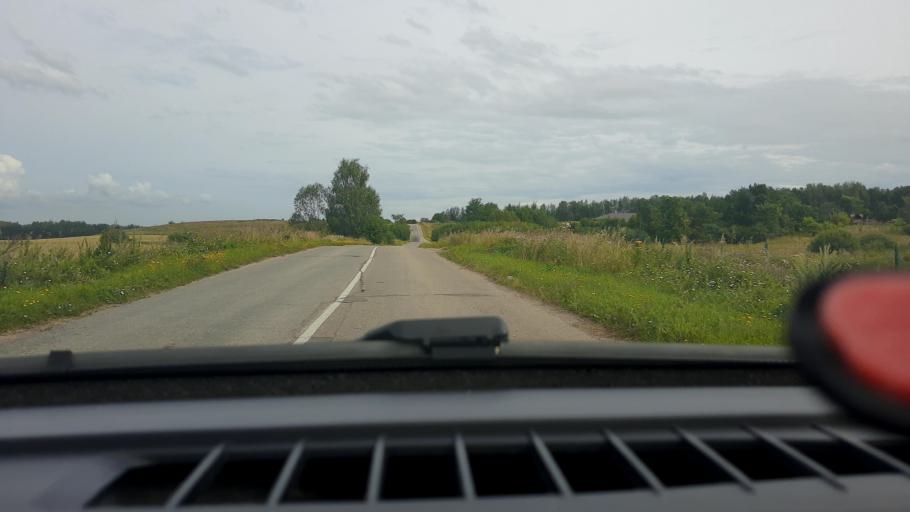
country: RU
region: Nizjnij Novgorod
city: Burevestnik
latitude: 56.0391
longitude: 43.7134
